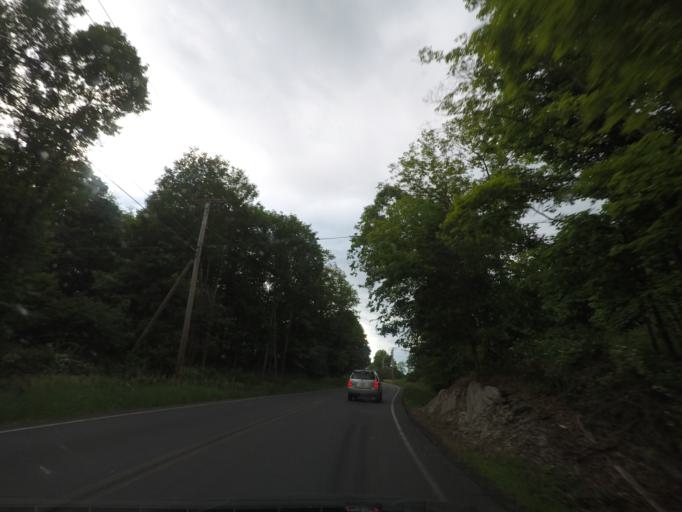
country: US
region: New York
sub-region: Dutchess County
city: Pine Plains
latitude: 41.9879
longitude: -73.6802
